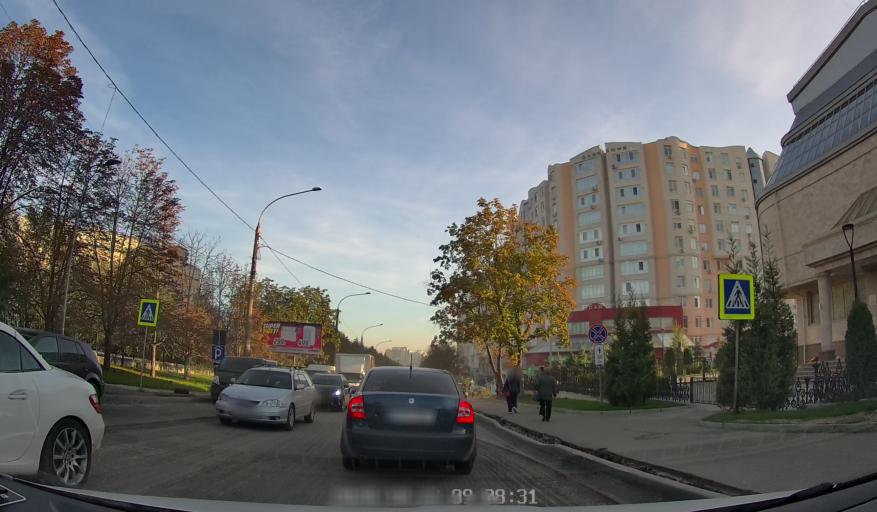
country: MD
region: Chisinau
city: Chisinau
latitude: 46.9958
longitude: 28.8329
